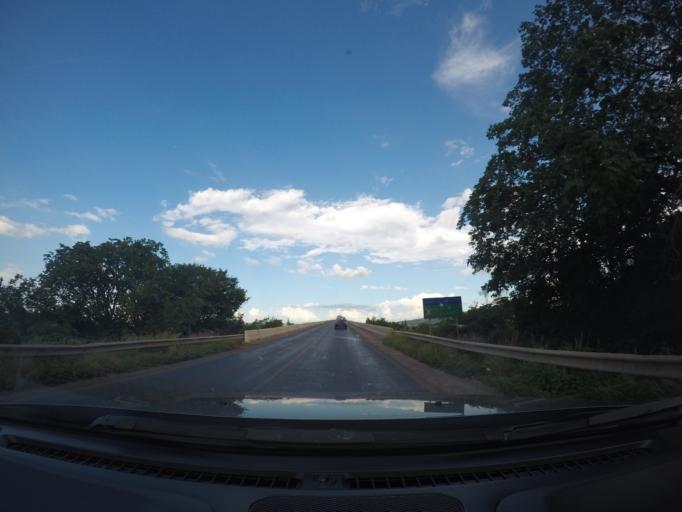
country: BR
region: Bahia
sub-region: Ibotirama
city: Ibotirama
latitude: -12.1818
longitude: -43.2311
